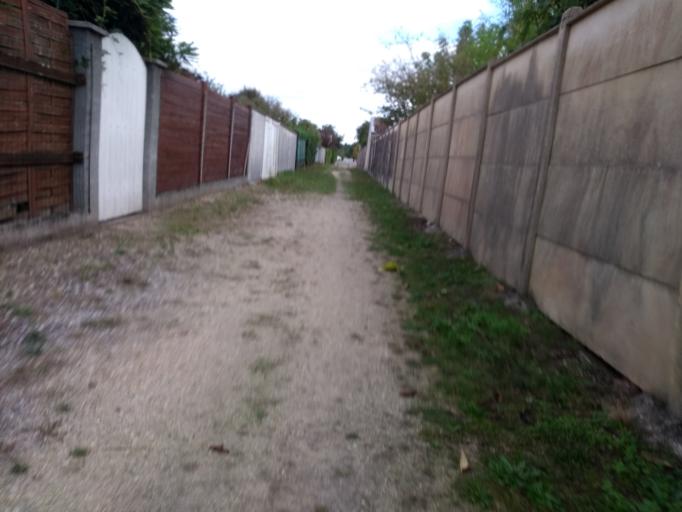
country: FR
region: Aquitaine
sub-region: Departement de la Gironde
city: Saint-Aubin-de-Medoc
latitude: 44.7676
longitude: -0.6984
